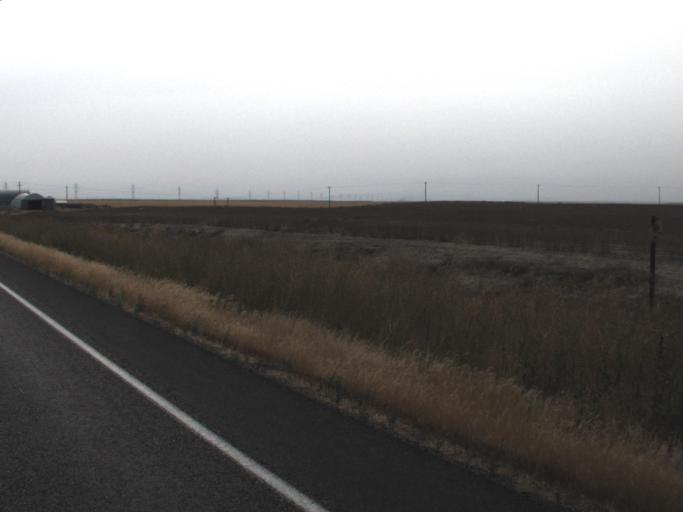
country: US
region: Washington
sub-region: Benton County
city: Benton City
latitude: 46.1063
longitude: -119.6018
